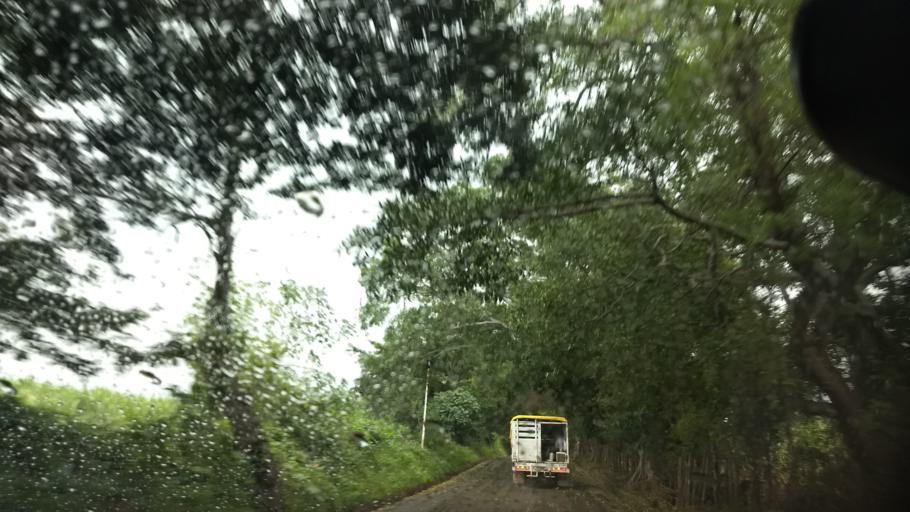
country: MX
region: Jalisco
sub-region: Tonila
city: San Marcos
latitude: 19.4419
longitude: -103.4941
